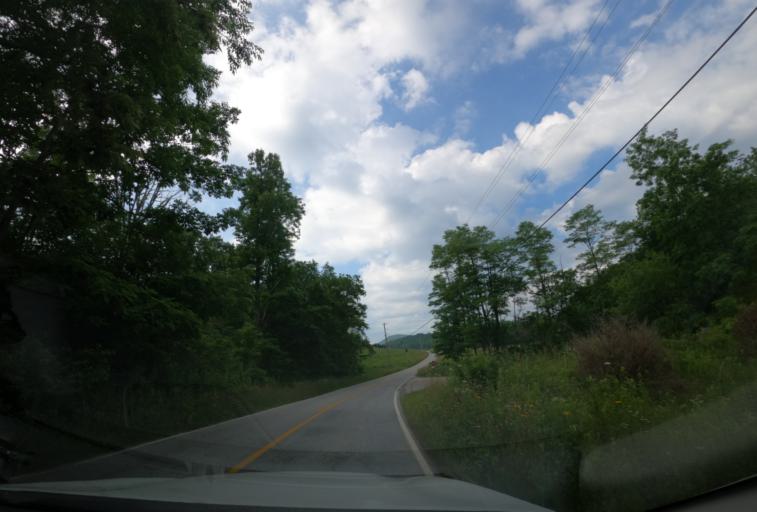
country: US
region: Georgia
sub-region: Rabun County
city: Mountain City
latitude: 35.0062
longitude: -83.3029
